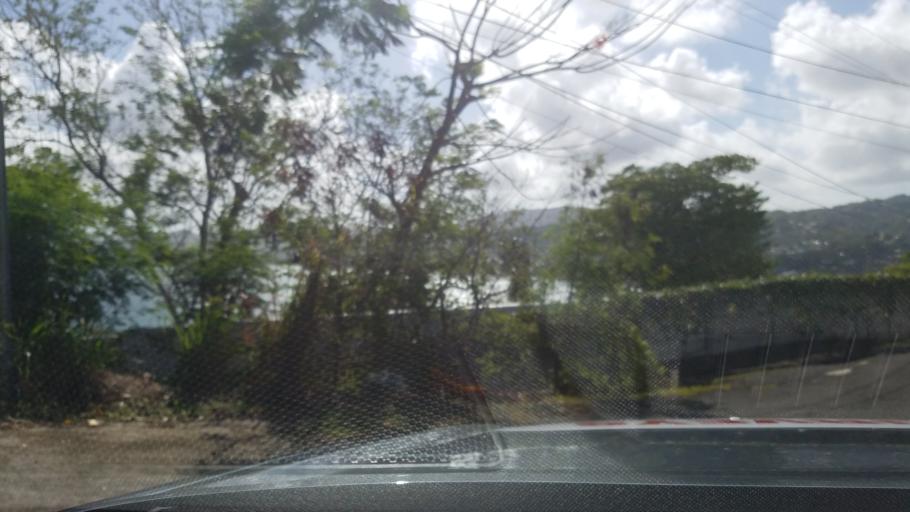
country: LC
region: Castries Quarter
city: Bisee
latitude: 14.0218
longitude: -61.0008
